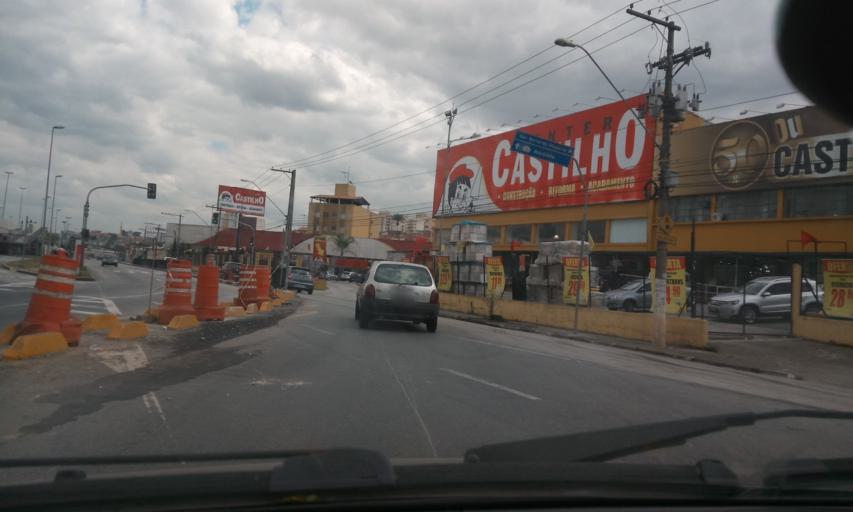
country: BR
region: Sao Paulo
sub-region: Sao Bernardo Do Campo
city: Sao Bernardo do Campo
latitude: -23.7222
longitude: -46.5412
